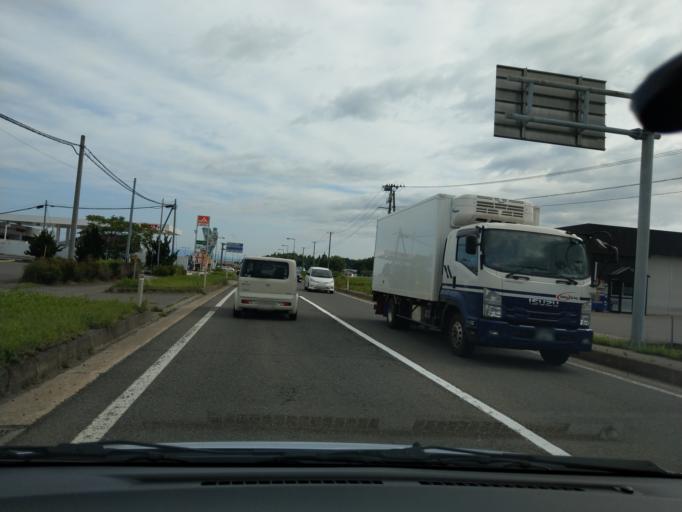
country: JP
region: Akita
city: Yokotemachi
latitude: 39.3777
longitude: 140.5682
